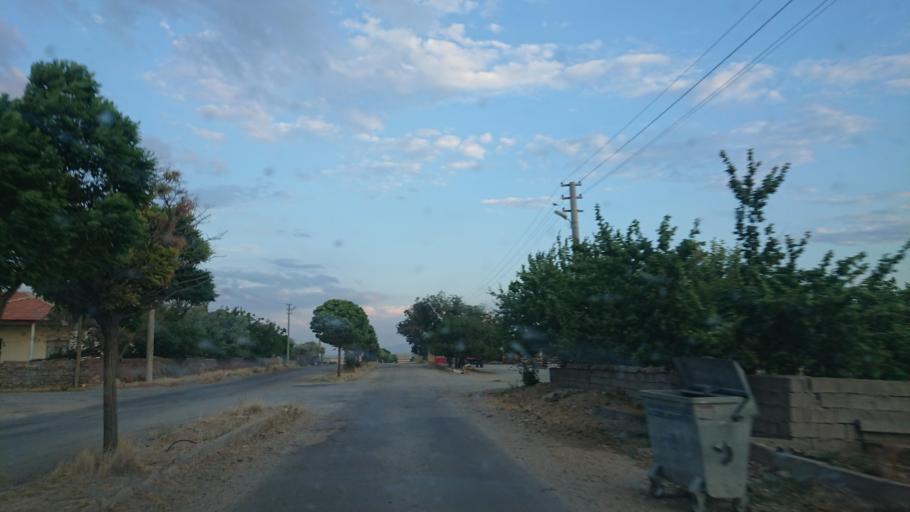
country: TR
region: Aksaray
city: Agacoren
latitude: 38.9215
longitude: 34.0349
